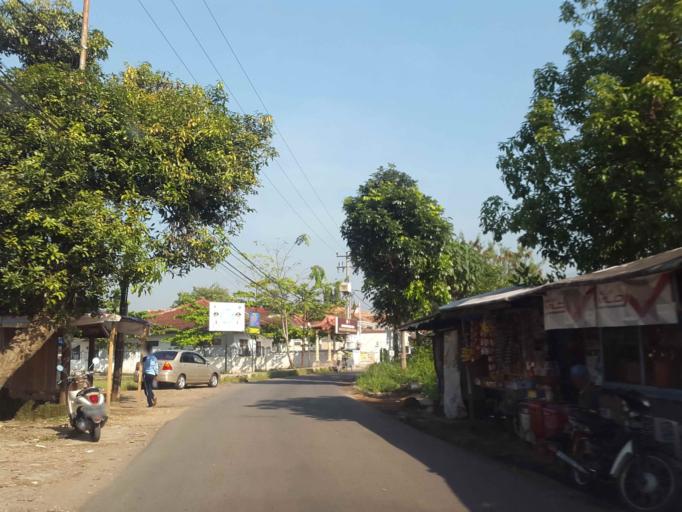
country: ID
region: West Java
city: Cibeber
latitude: -6.8697
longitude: 107.0955
